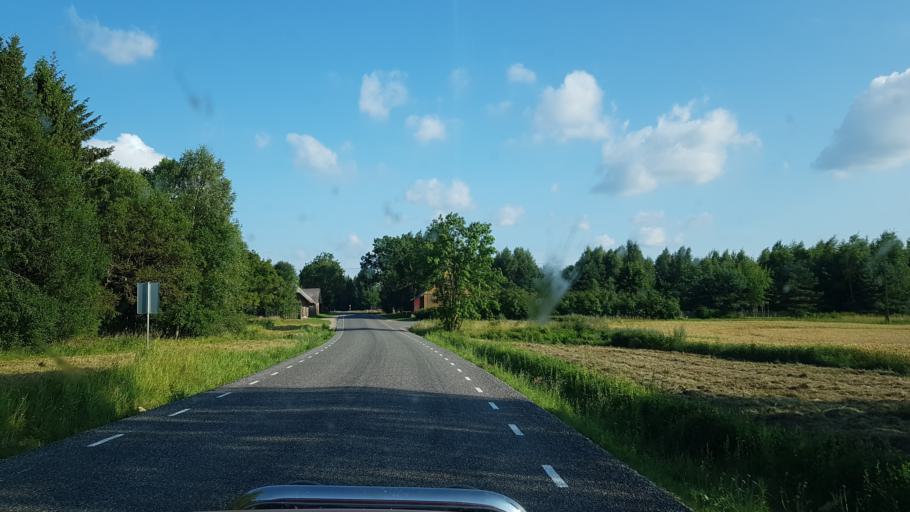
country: EE
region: Polvamaa
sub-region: Polva linn
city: Polva
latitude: 58.0033
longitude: 26.9268
